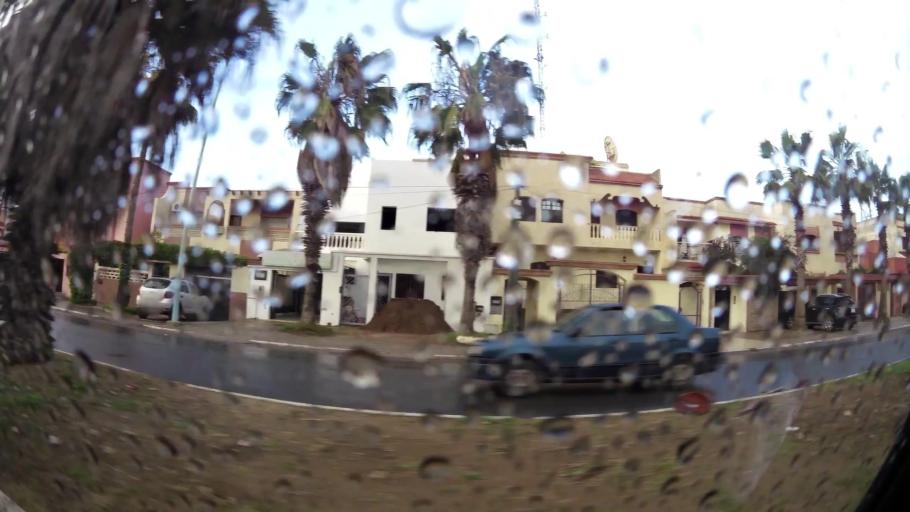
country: MA
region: Doukkala-Abda
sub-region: El-Jadida
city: El Jadida
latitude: 33.2312
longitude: -8.4990
